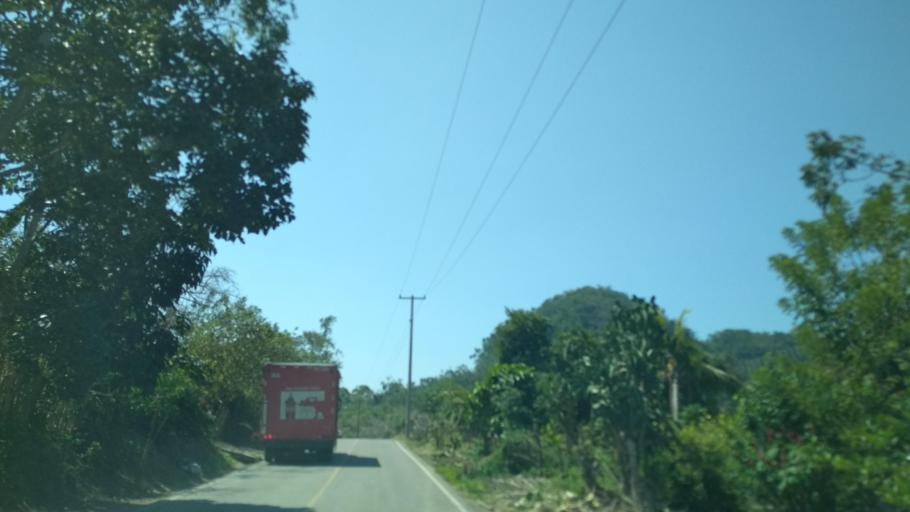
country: MX
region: Veracruz
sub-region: Papantla
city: Polutla
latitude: 20.4739
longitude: -97.2166
